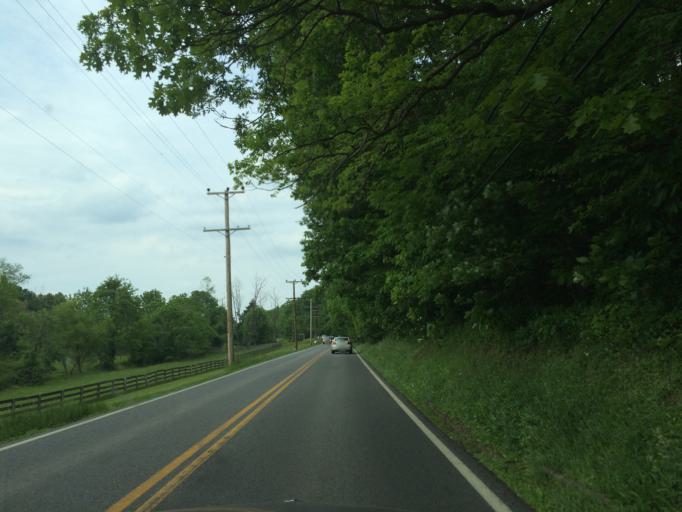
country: US
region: Maryland
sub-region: Howard County
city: Columbia
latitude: 39.2781
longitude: -76.9007
